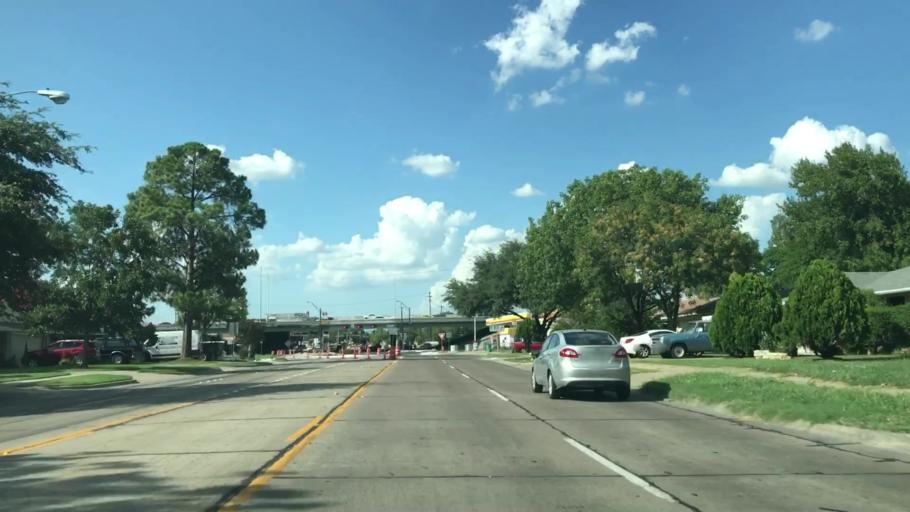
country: US
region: Texas
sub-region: Dallas County
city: Irving
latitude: 32.8349
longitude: -96.9510
